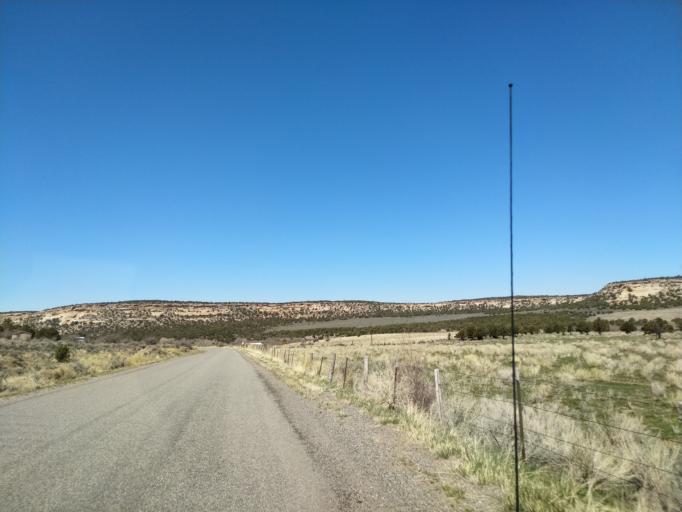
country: US
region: Colorado
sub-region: Mesa County
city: Loma
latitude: 38.9600
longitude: -109.0063
